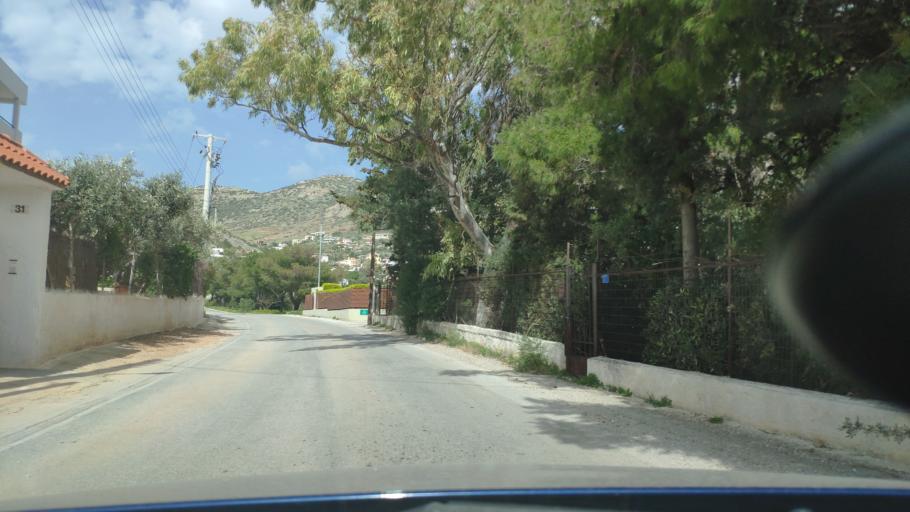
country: GR
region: Attica
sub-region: Nomarchia Anatolikis Attikis
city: Limin Mesoyaias
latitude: 37.8963
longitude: 24.0238
